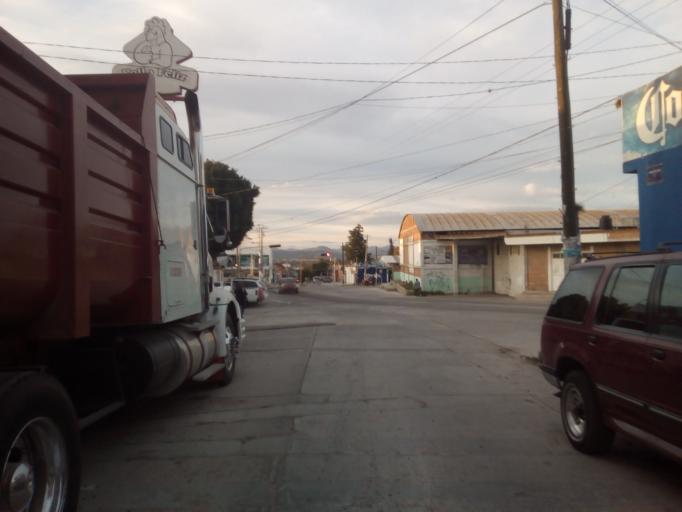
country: MX
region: Guerrero
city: San Luis de la Paz
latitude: 21.2912
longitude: -100.5137
